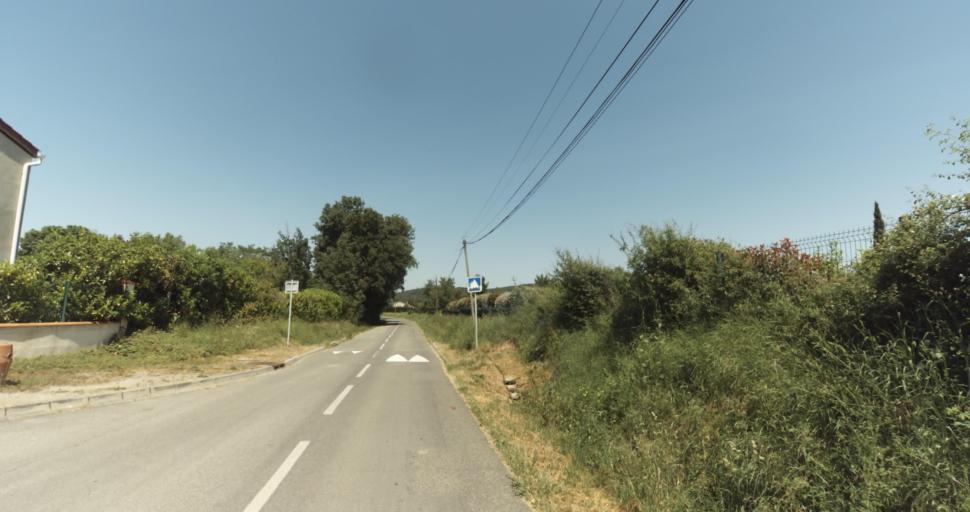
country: FR
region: Midi-Pyrenees
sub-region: Departement de la Haute-Garonne
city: Levignac
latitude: 43.6409
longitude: 1.1733
